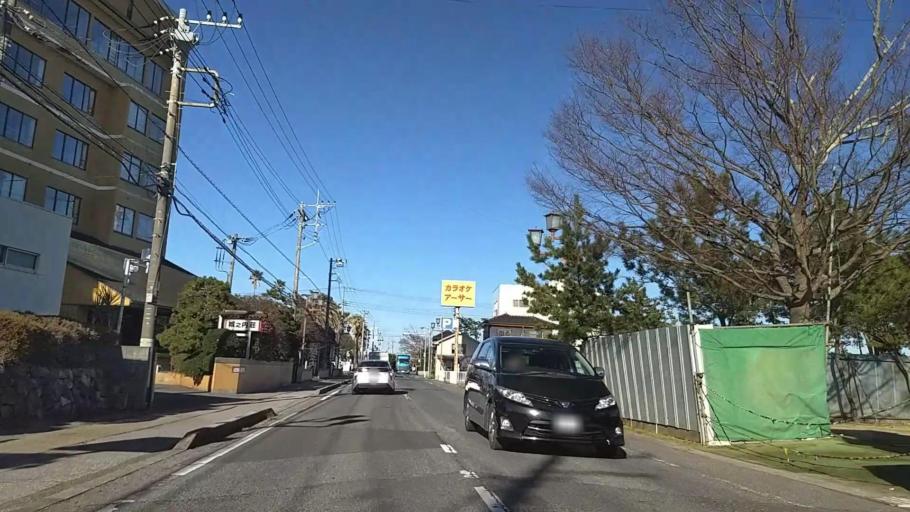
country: JP
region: Chiba
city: Mobara
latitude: 35.4304
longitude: 140.3961
